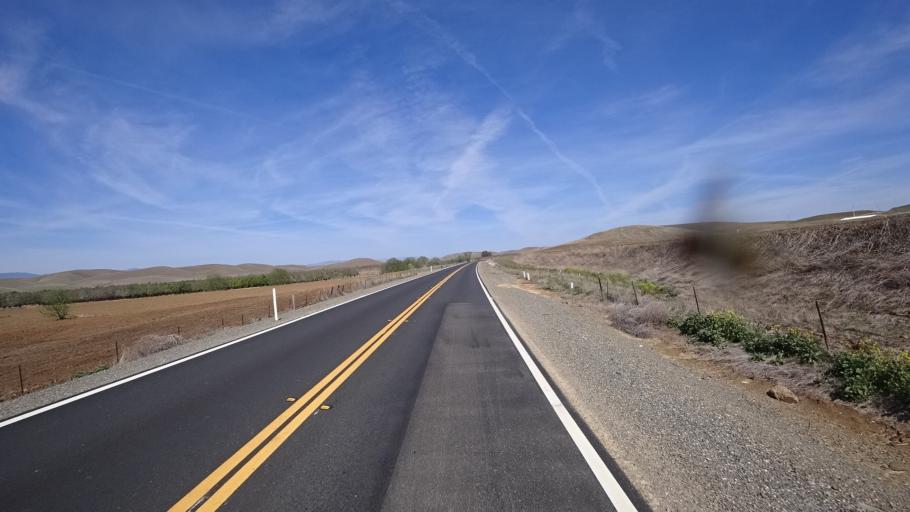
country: US
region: California
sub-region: Glenn County
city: Willows
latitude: 39.5330
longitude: -122.3417
